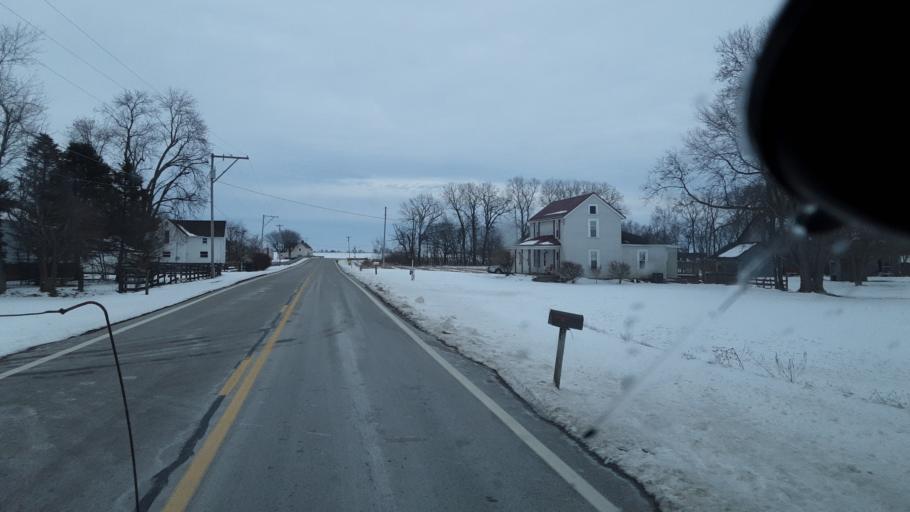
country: US
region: Ohio
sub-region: Pickaway County
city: Williamsport
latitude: 39.6604
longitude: -83.1293
